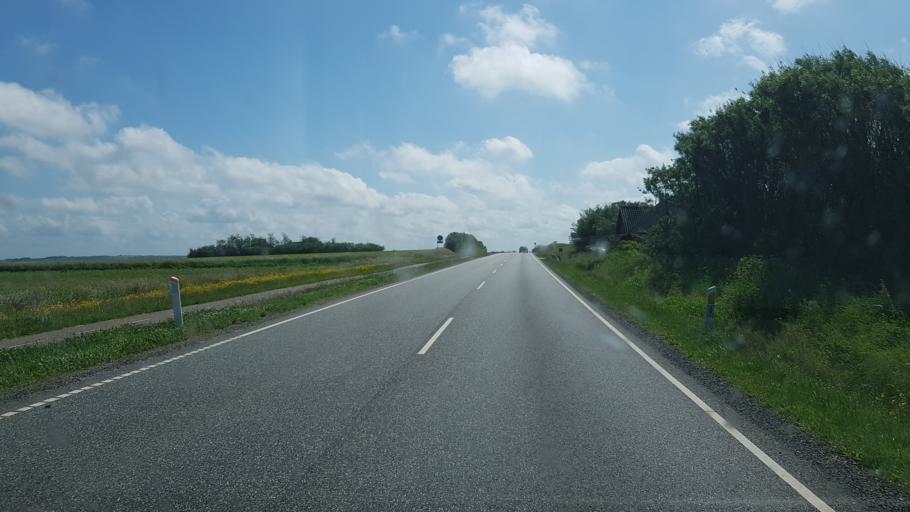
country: DK
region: Central Jutland
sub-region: Lemvig Kommune
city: Lemvig
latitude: 56.5524
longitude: 8.2518
